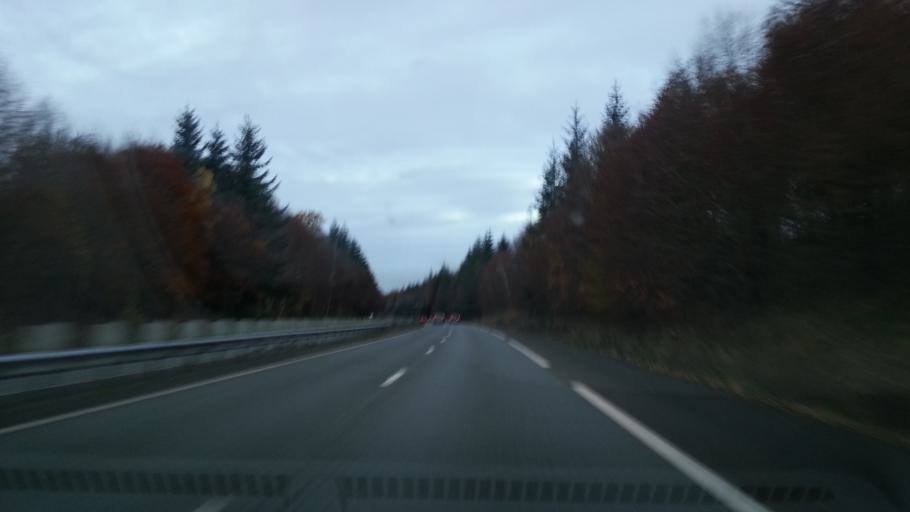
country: FR
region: Picardie
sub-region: Departement de l'Oise
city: Agnetz
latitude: 49.4033
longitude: 2.3687
